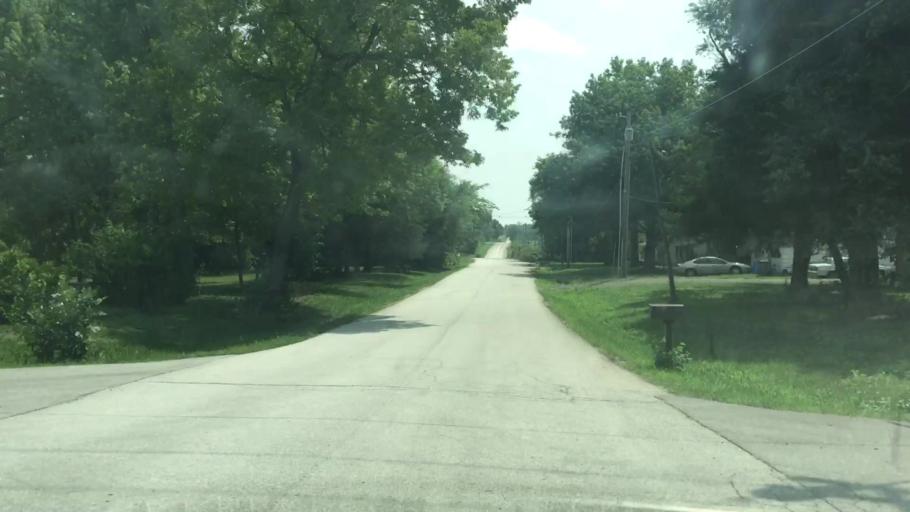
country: US
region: Kansas
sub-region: Douglas County
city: Baldwin City
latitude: 38.7731
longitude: -95.2049
